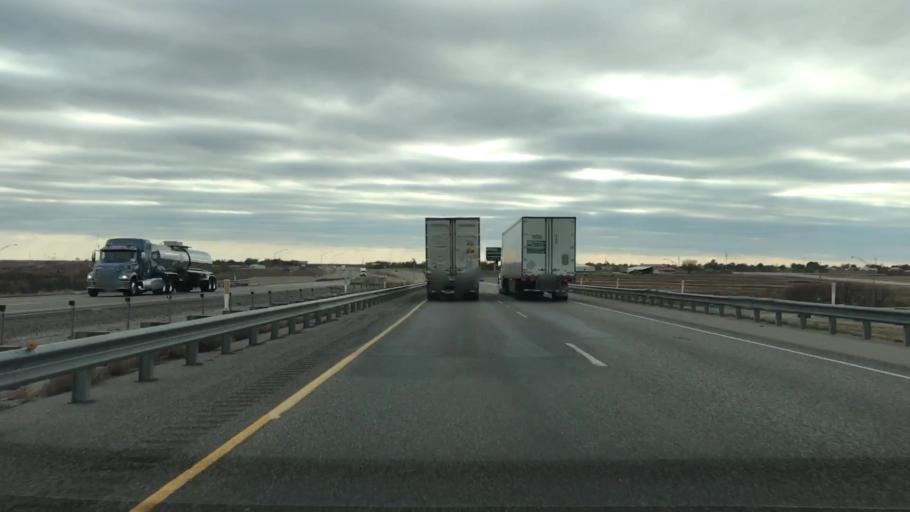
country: US
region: Oklahoma
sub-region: Beckham County
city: Sayre
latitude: 35.3167
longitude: -99.6121
